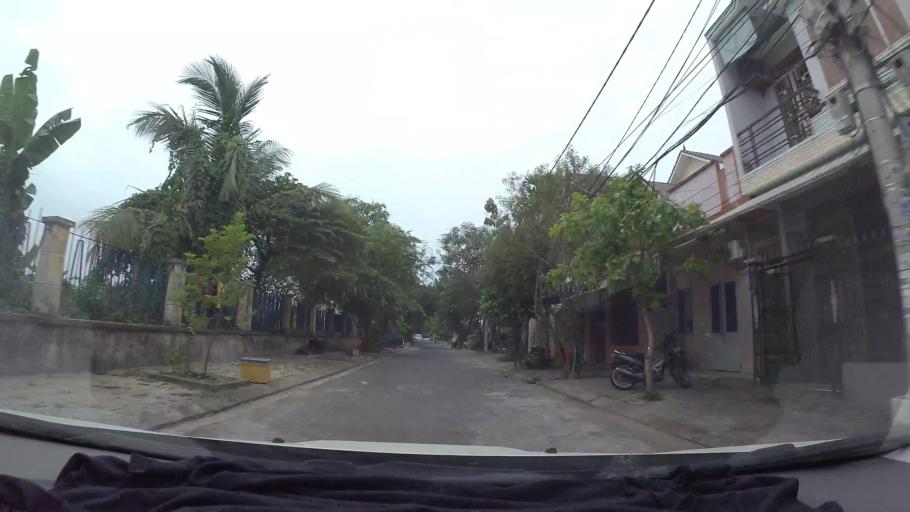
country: VN
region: Da Nang
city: Thanh Khe
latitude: 16.0612
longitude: 108.1839
